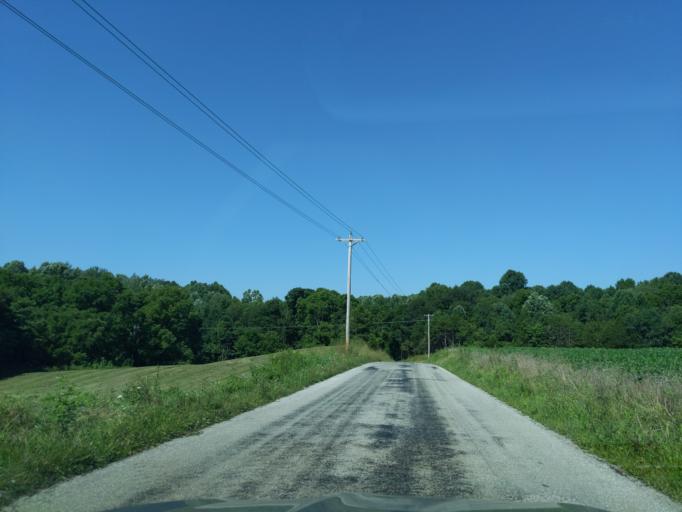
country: US
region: Indiana
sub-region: Decatur County
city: Westport
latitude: 39.1128
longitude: -85.4400
